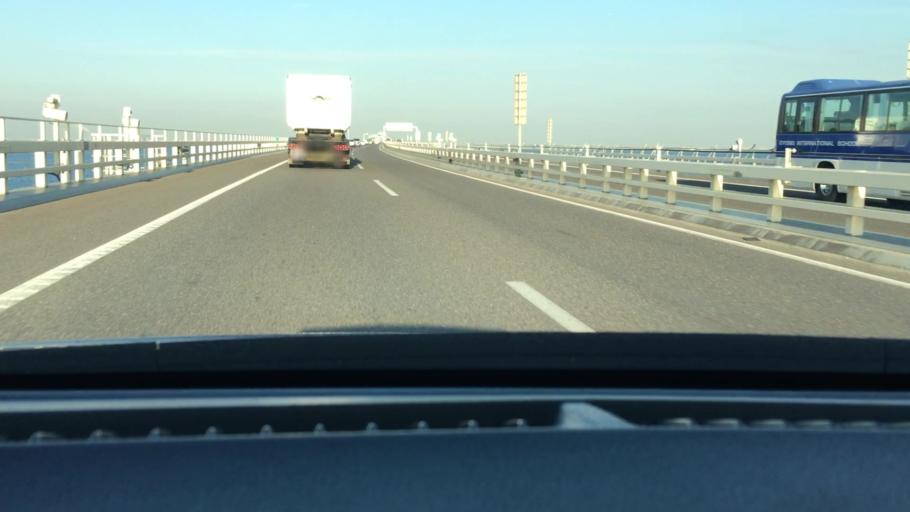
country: JP
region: Chiba
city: Kisarazu
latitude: 35.4387
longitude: 139.9118
